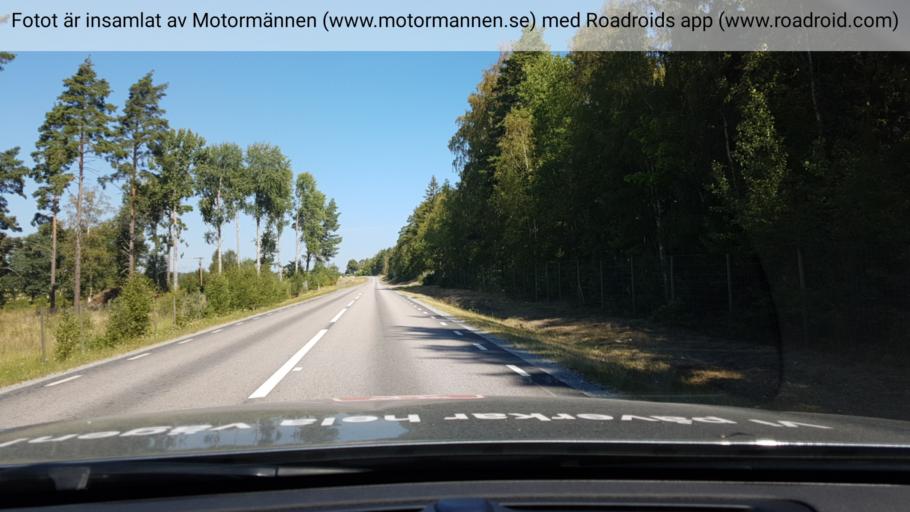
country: SE
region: Stockholm
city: Stenhamra
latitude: 59.3360
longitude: 17.6408
